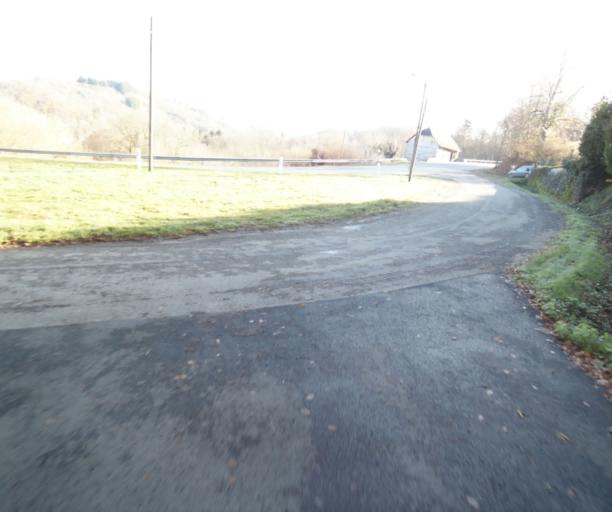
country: FR
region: Limousin
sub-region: Departement de la Correze
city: Laguenne
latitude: 45.2418
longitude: 1.7716
